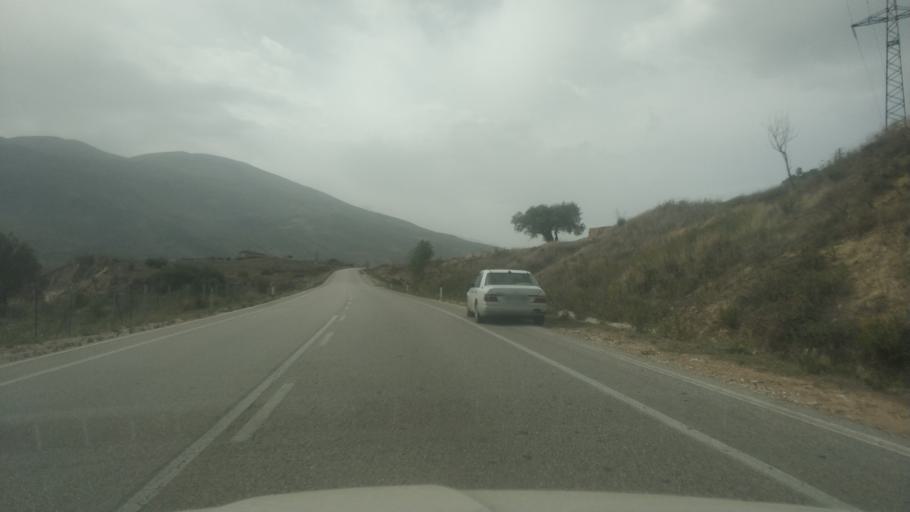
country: AL
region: Gjirokaster
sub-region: Rrethi i Tepelenes
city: Memaliaj
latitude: 40.3559
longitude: 19.9439
